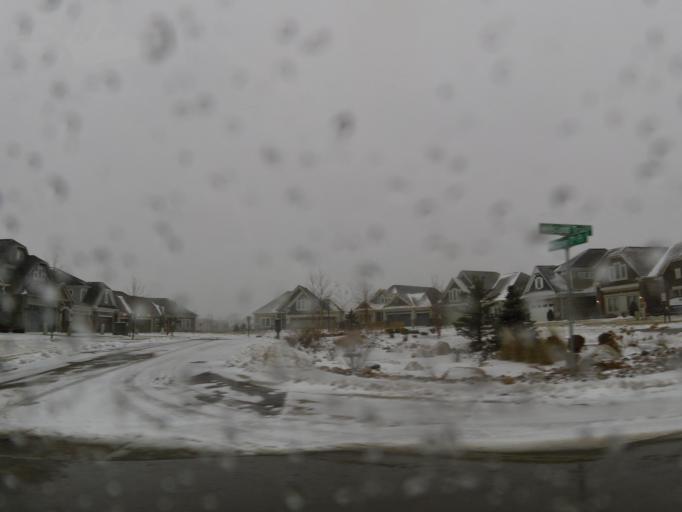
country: US
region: Minnesota
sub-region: Washington County
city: Oakdale
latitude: 44.9586
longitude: -92.9289
